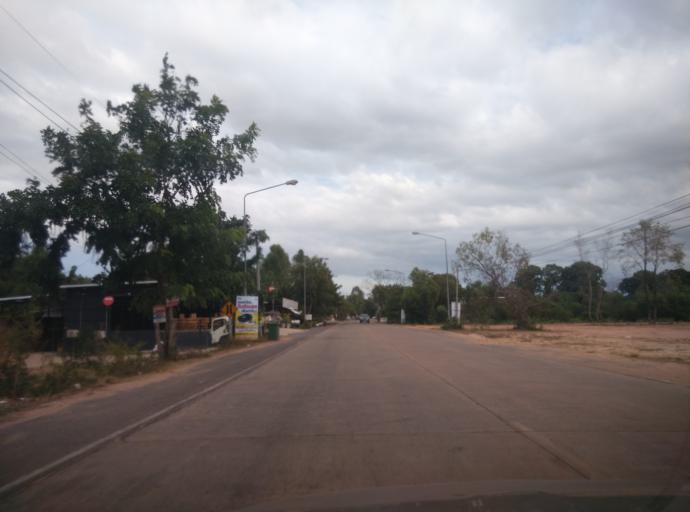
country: TH
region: Sisaket
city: Si Sa Ket
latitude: 15.1223
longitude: 104.3406
